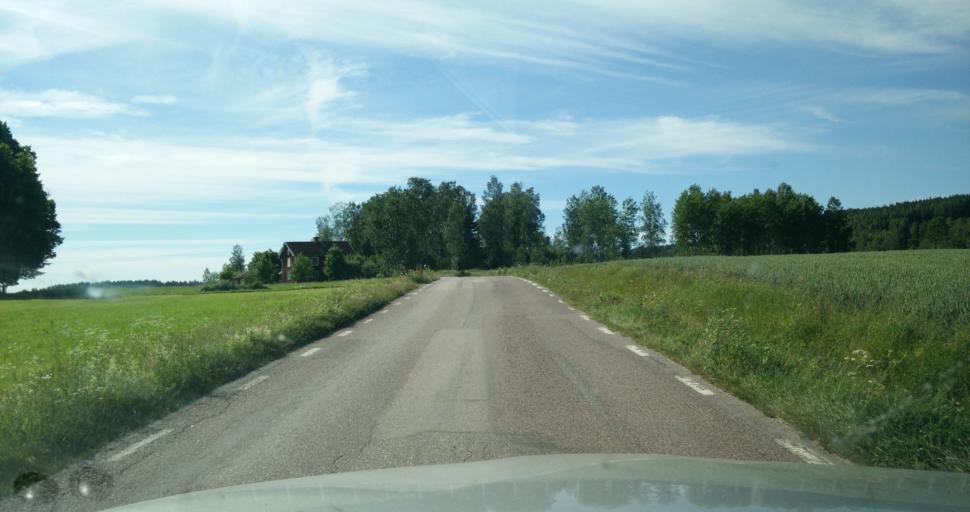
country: SE
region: Dalarna
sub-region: Hedemora Kommun
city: Langshyttan
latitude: 60.3934
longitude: 15.9559
